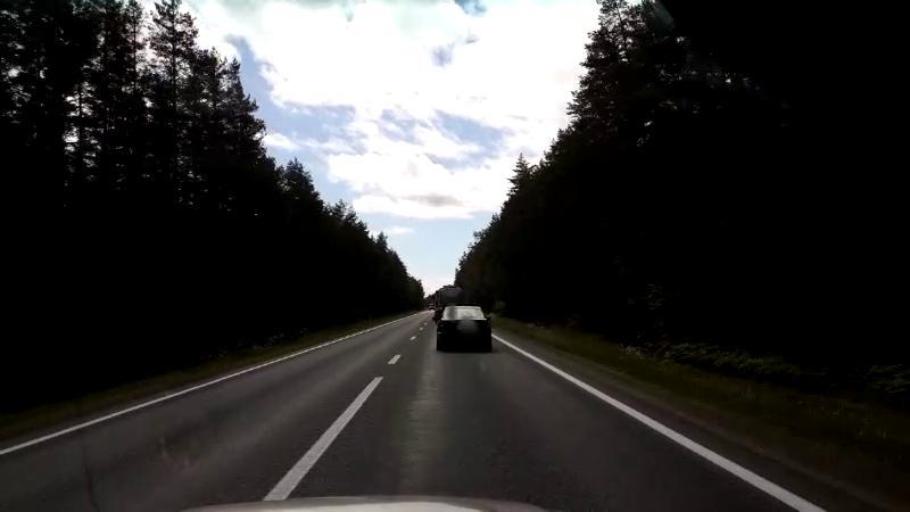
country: LV
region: Salacgrivas
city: Salacgriva
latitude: 57.5325
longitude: 24.4310
